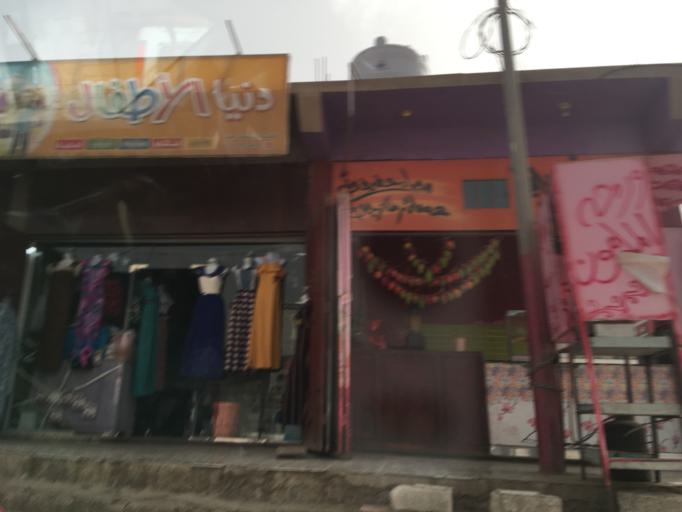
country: YE
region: Ad Dali'
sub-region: Ad Dhale'e
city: Dhalie
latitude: 13.7044
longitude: 44.7353
